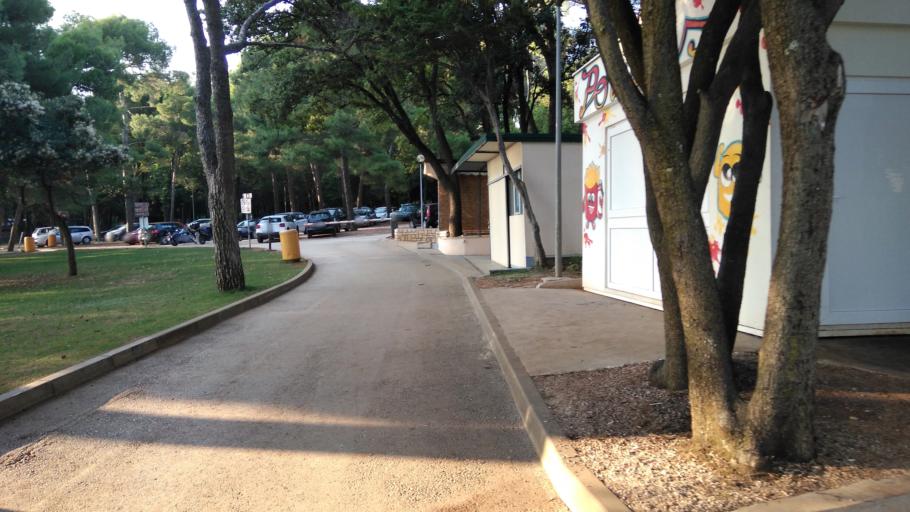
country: HR
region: Istarska
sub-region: Grad Porec
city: Porec
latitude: 45.1961
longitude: 13.5831
